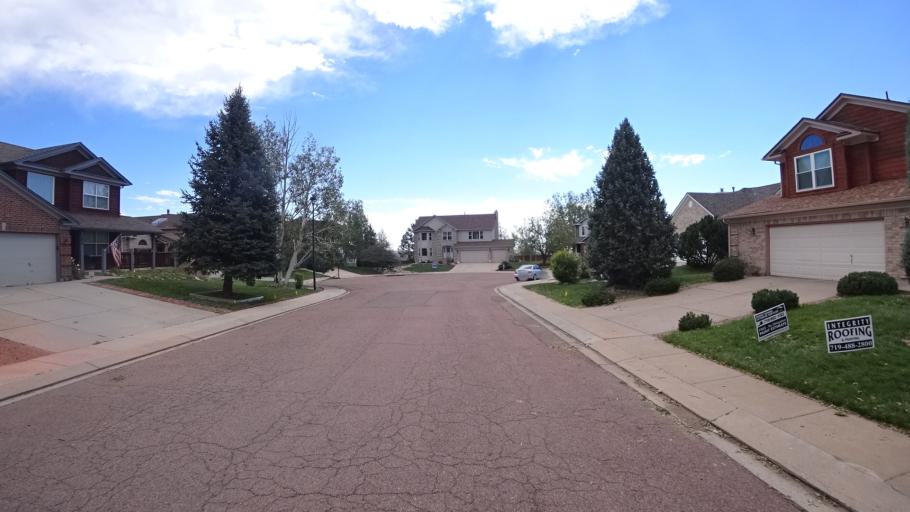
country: US
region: Colorado
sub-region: El Paso County
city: Fort Carson
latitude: 38.7628
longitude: -104.8149
